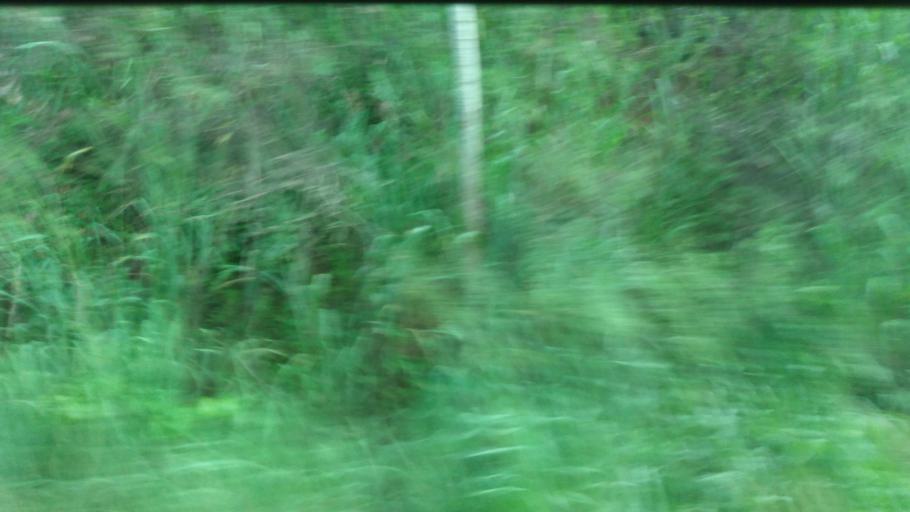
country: BR
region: Pernambuco
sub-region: Catende
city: Catende
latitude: -8.6933
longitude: -35.6993
